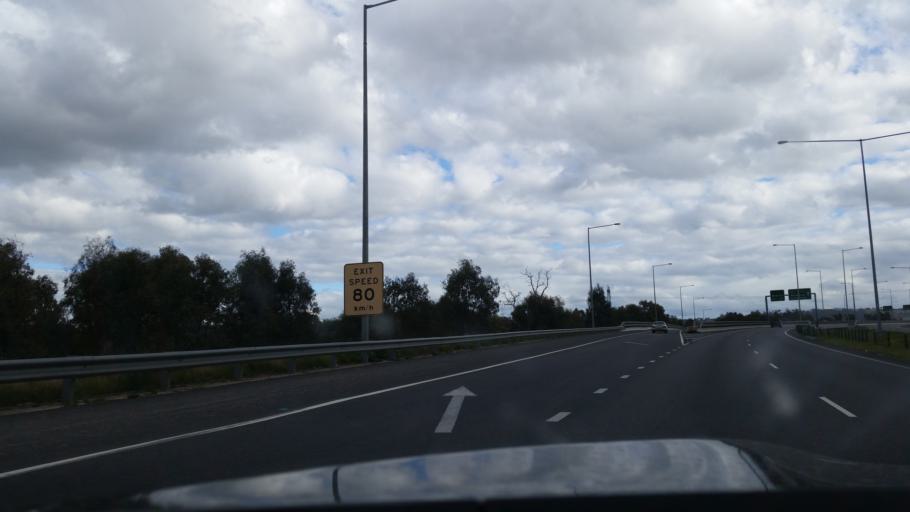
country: AU
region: Victoria
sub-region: Wodonga
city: Wodonga
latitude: -36.1078
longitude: 146.9029
